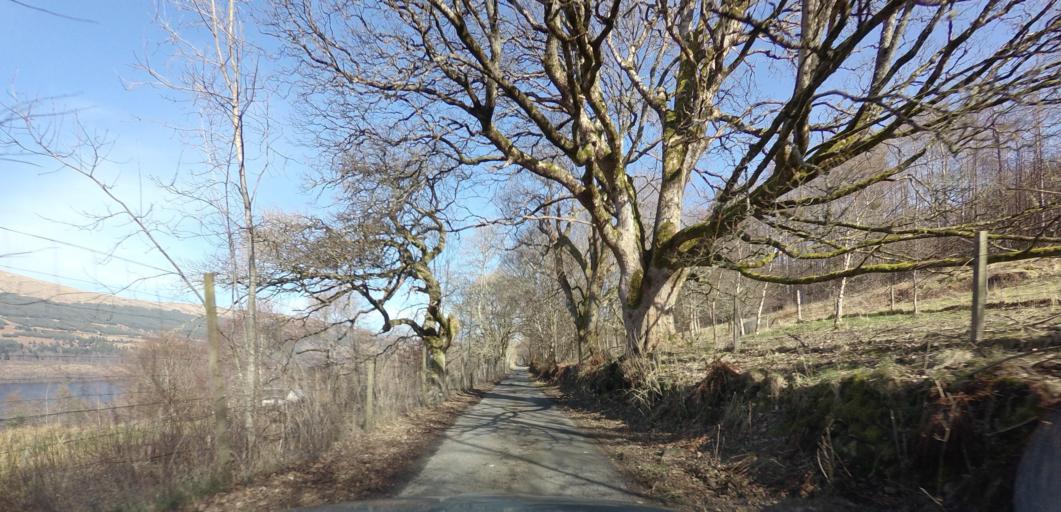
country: GB
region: Scotland
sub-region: Perth and Kinross
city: Comrie
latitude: 56.5413
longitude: -4.1017
